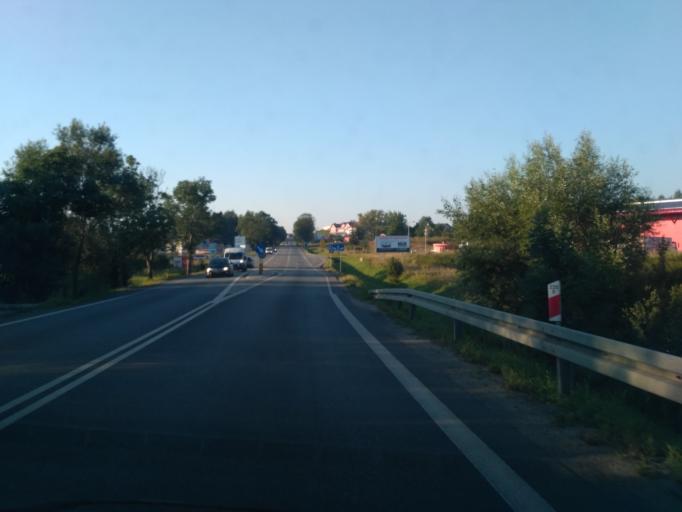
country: PL
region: Subcarpathian Voivodeship
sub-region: Krosno
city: Krosno
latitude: 49.6648
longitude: 21.7779
